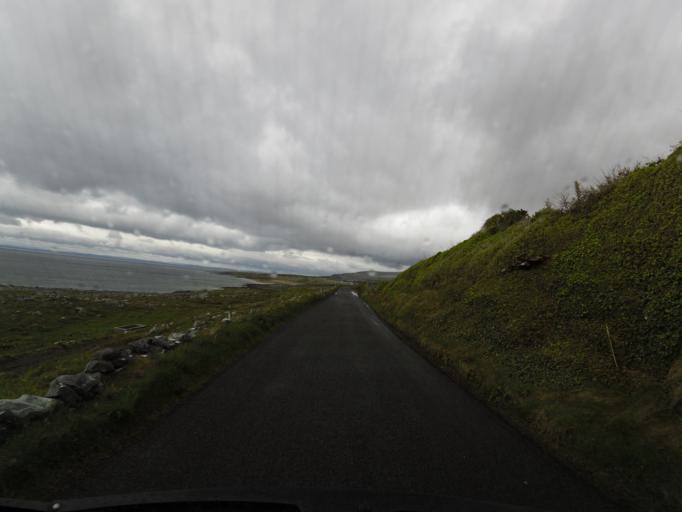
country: IE
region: Connaught
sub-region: County Galway
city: Bearna
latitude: 53.1092
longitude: -9.2929
